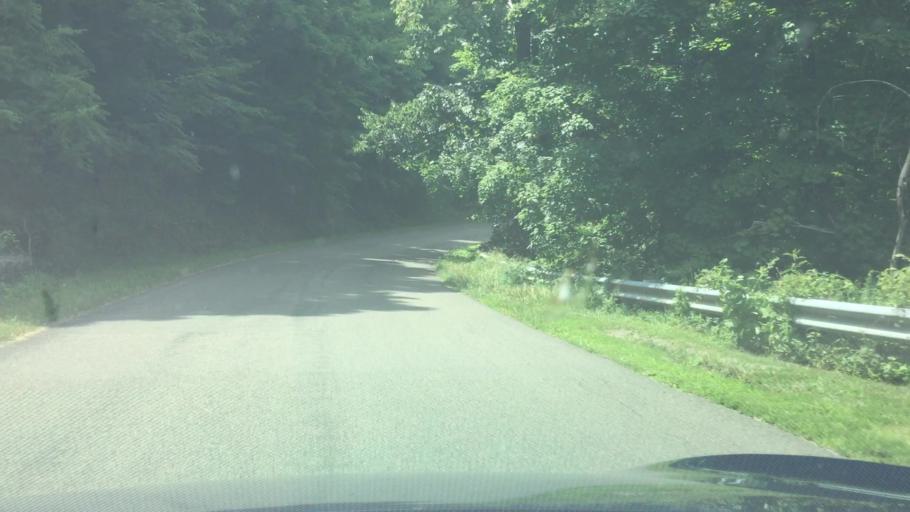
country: US
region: Virginia
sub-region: Wythe County
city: Wytheville
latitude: 36.9293
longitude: -81.0671
